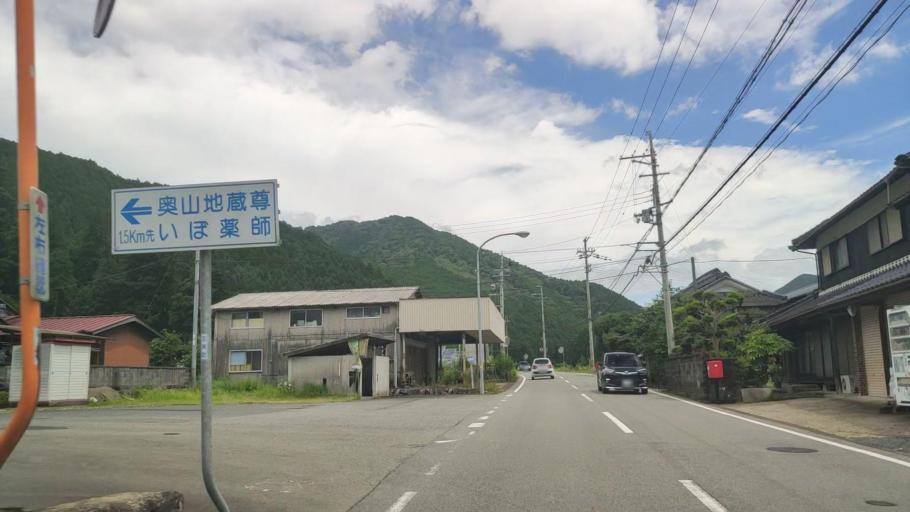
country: JP
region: Hyogo
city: Nishiwaki
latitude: 35.1702
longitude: 134.9298
